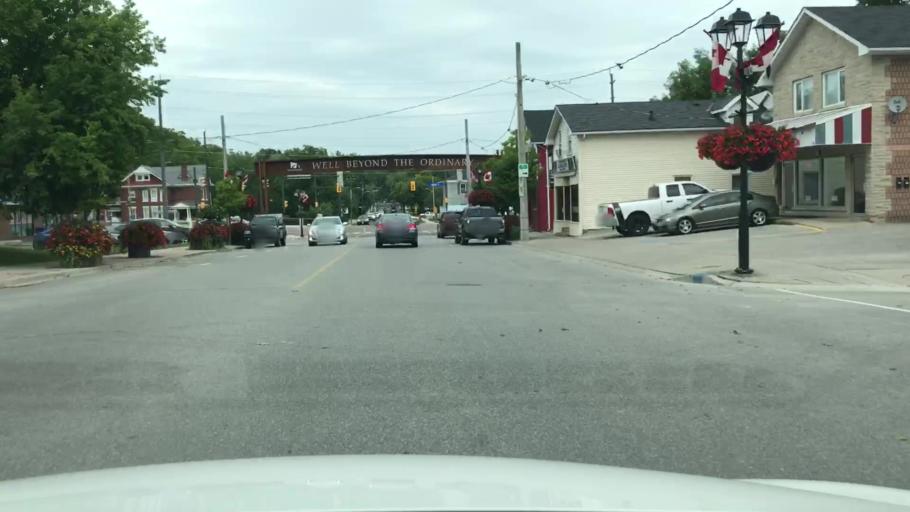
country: CA
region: Ontario
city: Newmarket
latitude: 44.0582
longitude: -79.4608
